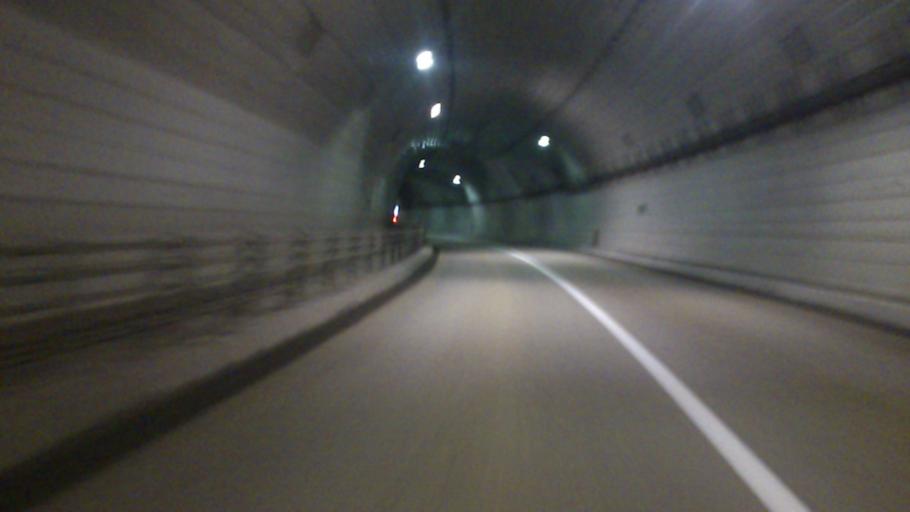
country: JP
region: Hokkaido
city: Kamikawa
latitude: 43.6745
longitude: 143.0352
